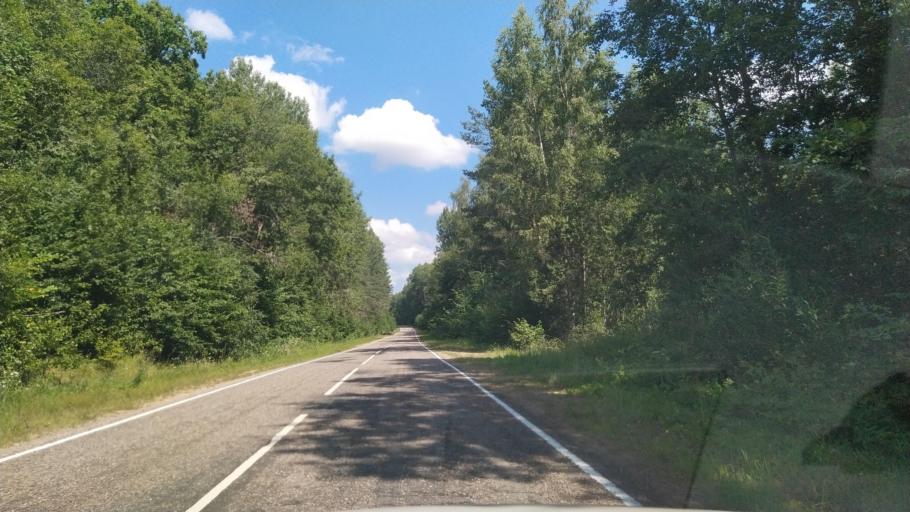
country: RU
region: Pskov
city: Pushkinskiye Gory
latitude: 57.0649
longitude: 28.9506
